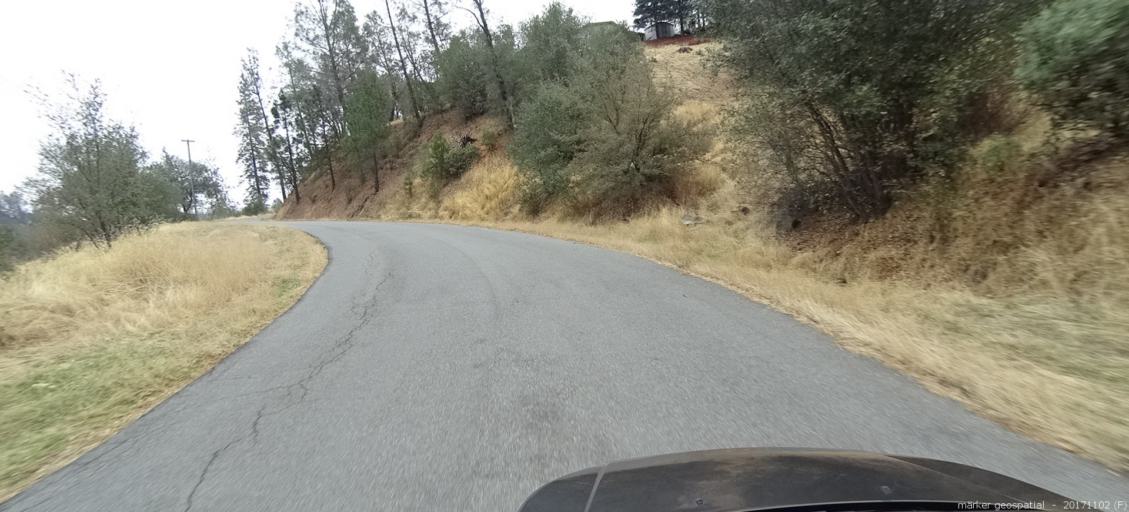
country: US
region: California
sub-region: Shasta County
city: Bella Vista
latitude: 40.7196
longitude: -122.2390
